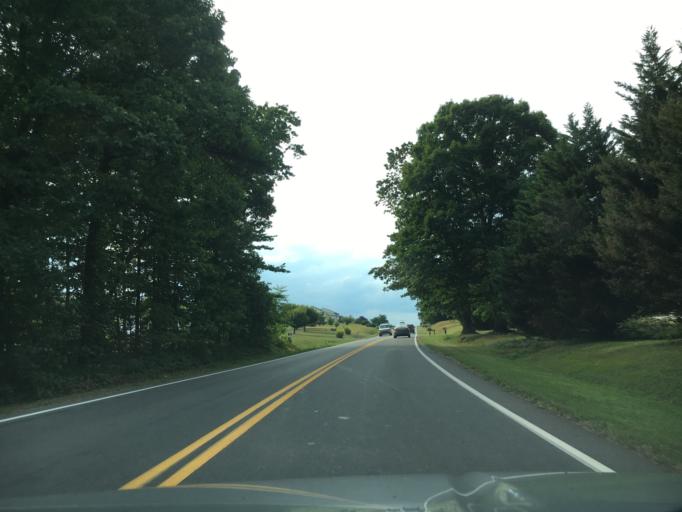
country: US
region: Virginia
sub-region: Campbell County
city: Rustburg
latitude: 37.2753
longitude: -79.1638
